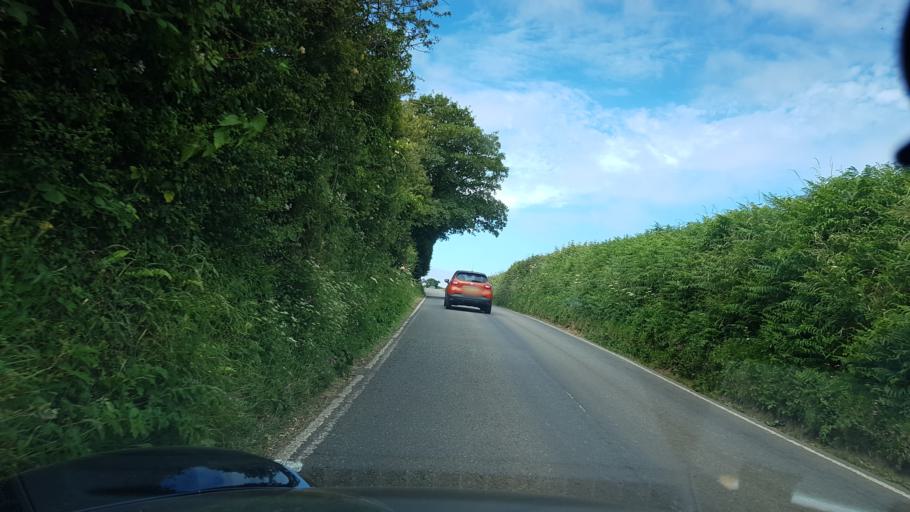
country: GB
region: Wales
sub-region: Pembrokeshire
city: Herbrandston
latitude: 51.7650
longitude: -5.0782
